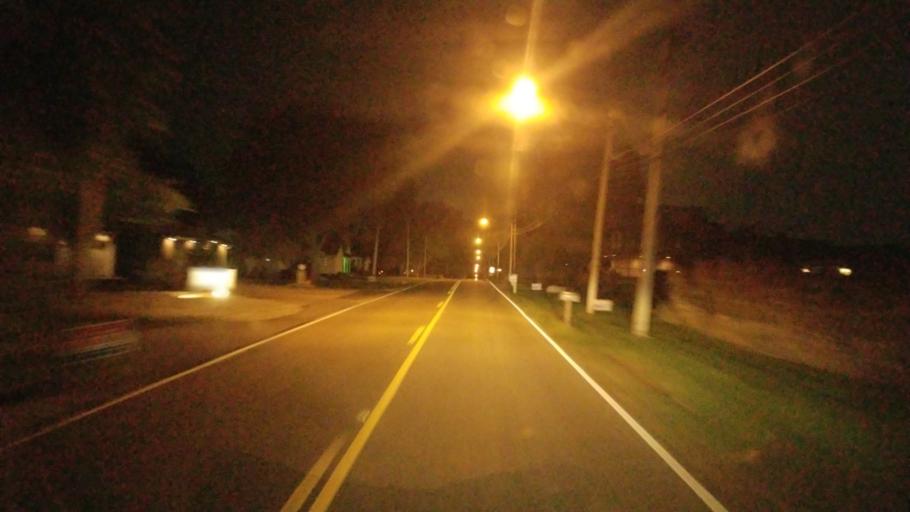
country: US
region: Ohio
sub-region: Stark County
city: Massillon
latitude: 40.7617
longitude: -81.5463
